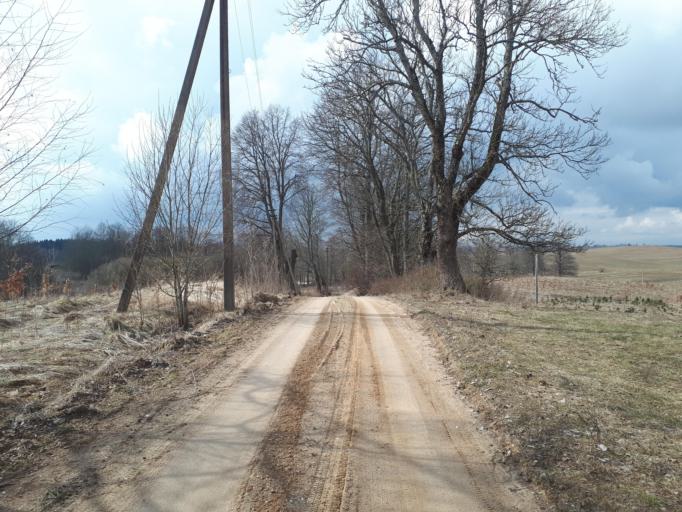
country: LT
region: Alytaus apskritis
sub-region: Alytaus rajonas
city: Daugai
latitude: 54.4108
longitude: 24.2967
